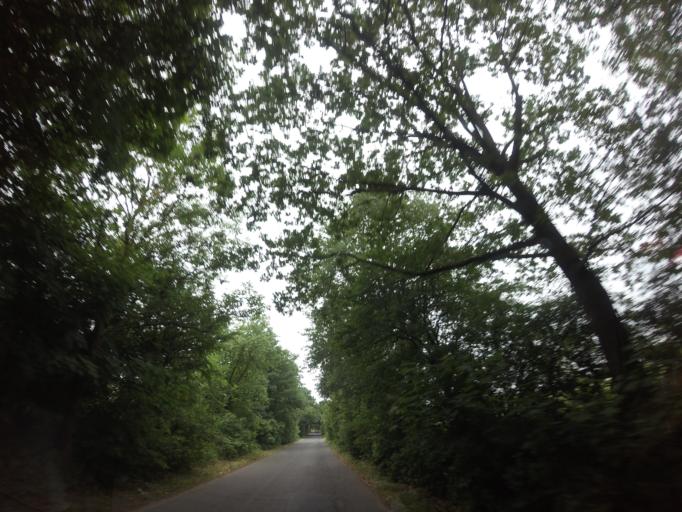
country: PL
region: West Pomeranian Voivodeship
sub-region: Powiat choszczenski
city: Bierzwnik
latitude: 53.1487
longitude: 15.6383
